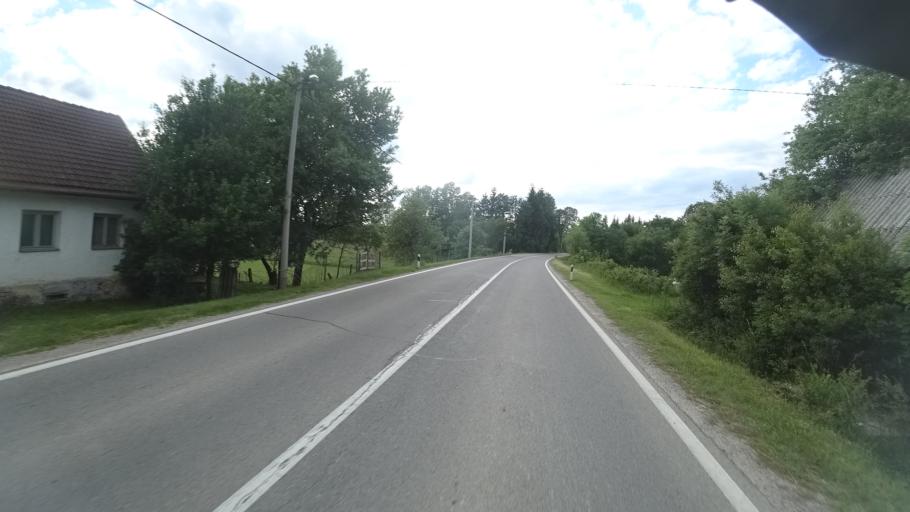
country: HR
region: Licko-Senjska
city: Gospic
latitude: 44.5163
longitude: 15.4189
